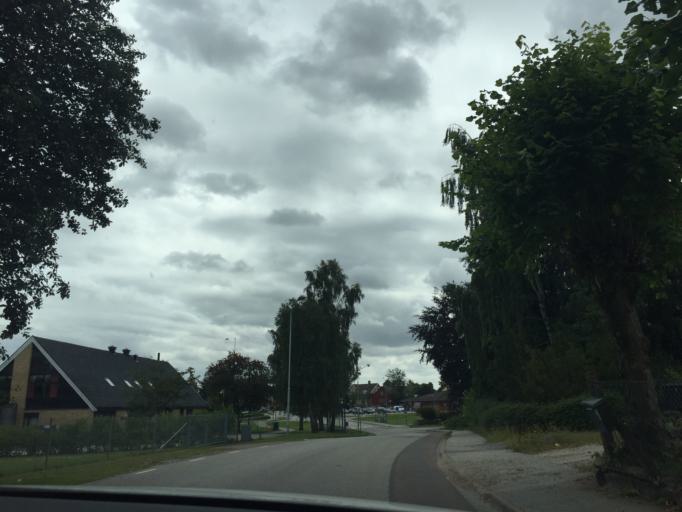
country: SE
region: Skane
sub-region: Sjobo Kommun
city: Blentarp
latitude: 55.5853
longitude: 13.6014
